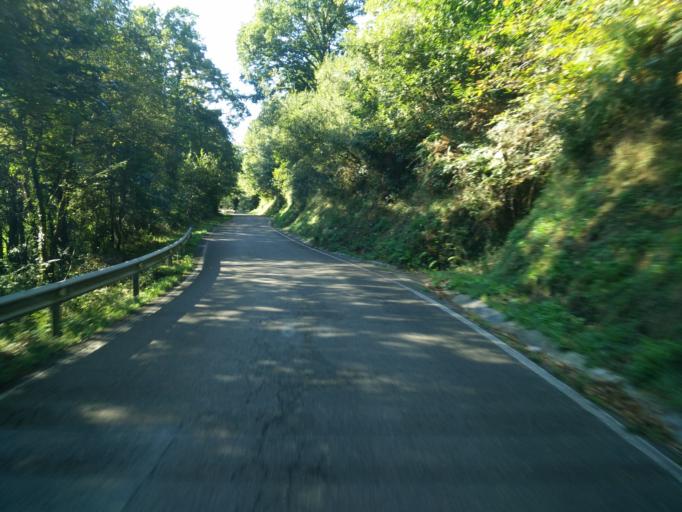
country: ES
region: Cantabria
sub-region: Provincia de Cantabria
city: San Pedro del Romeral
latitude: 43.1531
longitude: -3.8213
